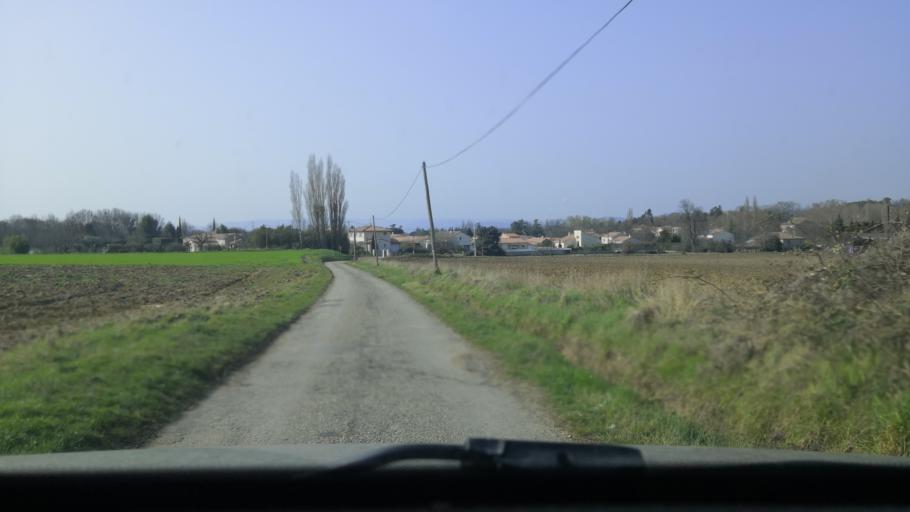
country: FR
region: Rhone-Alpes
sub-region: Departement de la Drome
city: La Begude-de-Mazenc
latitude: 44.5401
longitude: 4.9405
